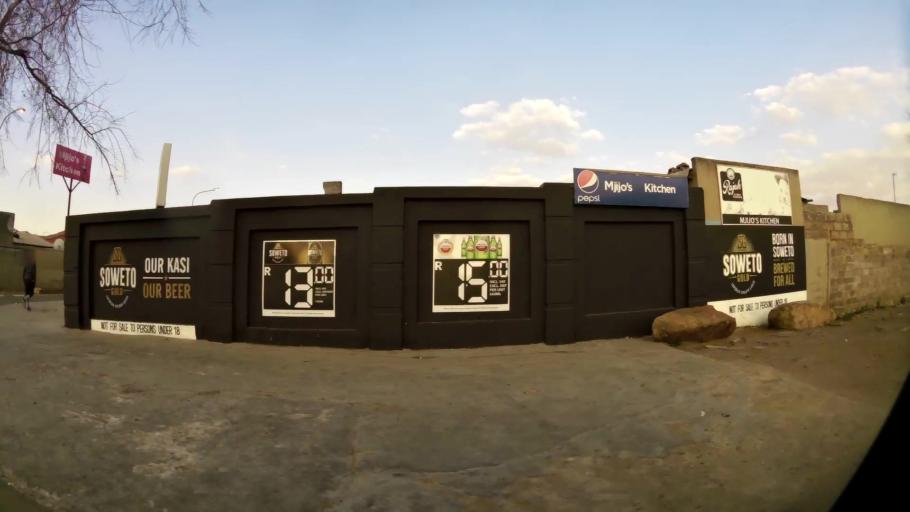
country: ZA
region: Gauteng
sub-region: City of Johannesburg Metropolitan Municipality
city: Roodepoort
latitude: -26.2170
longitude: 27.8933
